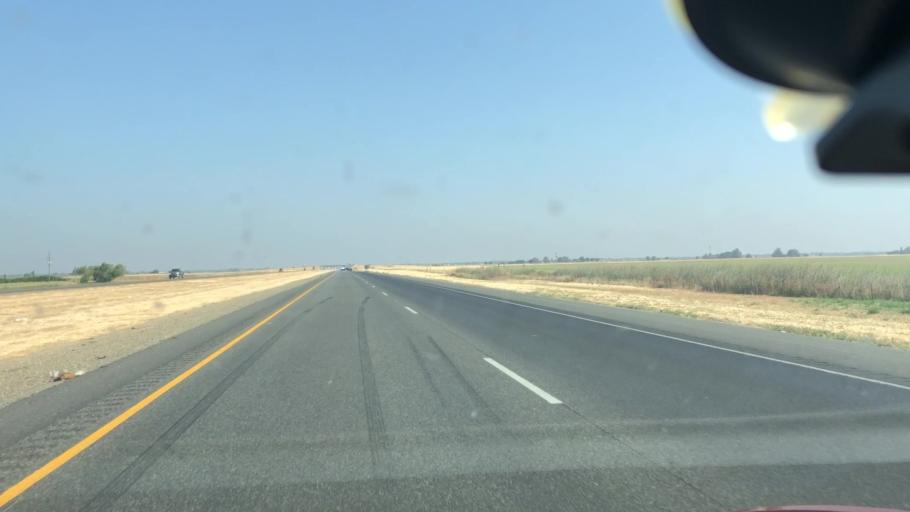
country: US
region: California
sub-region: Sacramento County
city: Laguna
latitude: 38.3583
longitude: -121.4731
